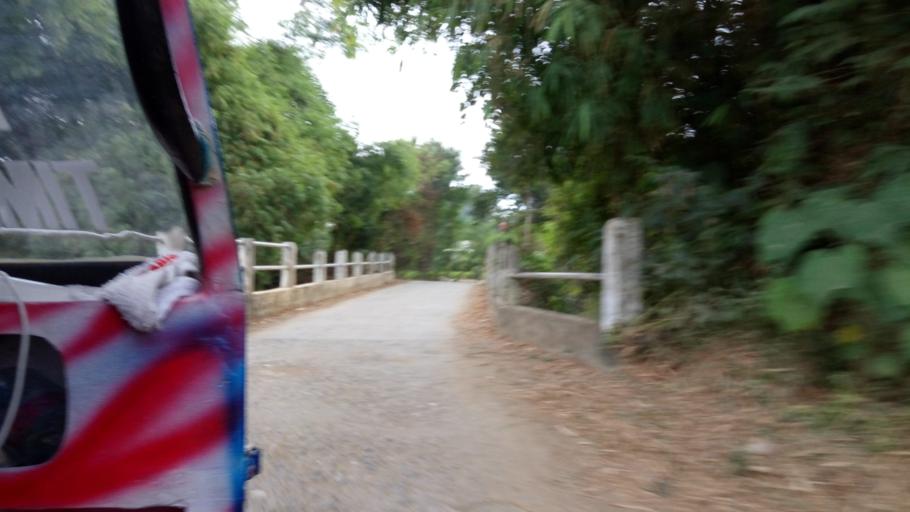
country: PH
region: Ilocos
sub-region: Province of La Union
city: Santo Tomas
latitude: 16.2884
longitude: 120.3799
